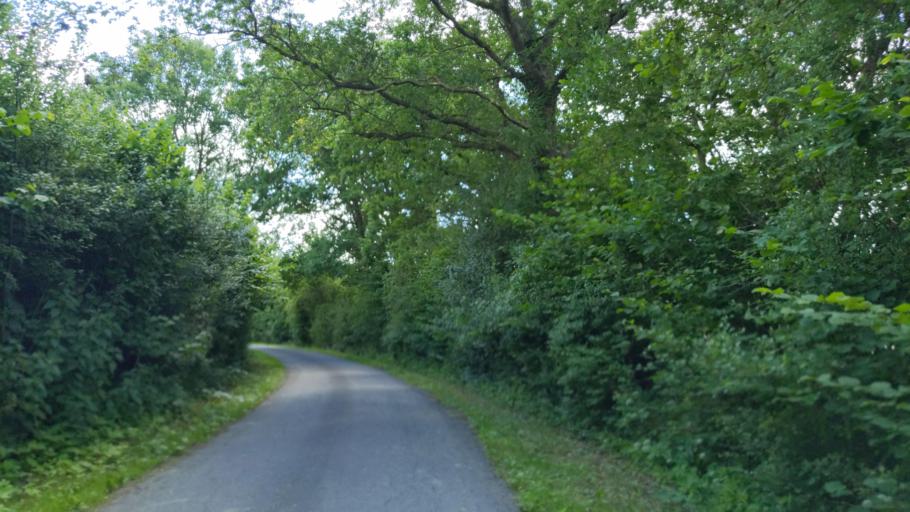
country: DE
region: Schleswig-Holstein
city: Stockelsdorf
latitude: 53.9444
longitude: 10.6490
